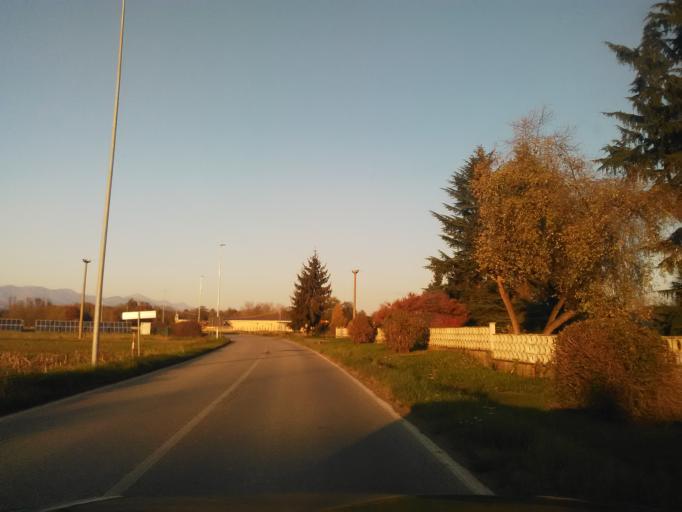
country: IT
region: Piedmont
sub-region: Provincia di Biella
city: Cerrione
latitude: 45.4731
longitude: 8.0701
